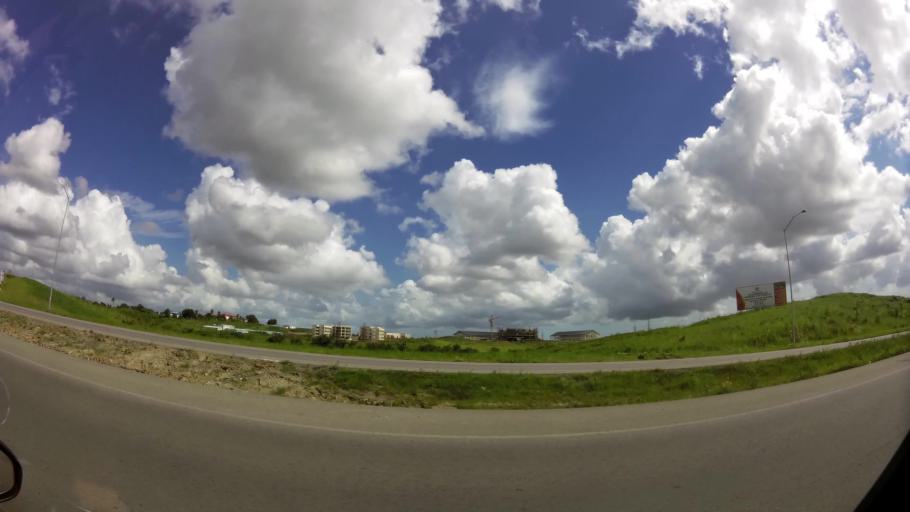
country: TT
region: Penal/Debe
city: Debe
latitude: 10.2262
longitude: -61.4498
